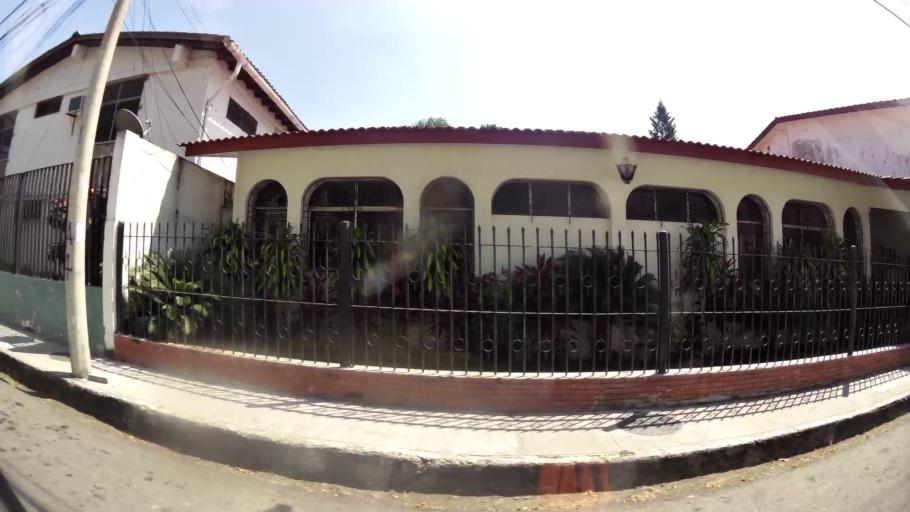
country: EC
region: Guayas
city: Guayaquil
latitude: -2.1689
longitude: -79.9144
